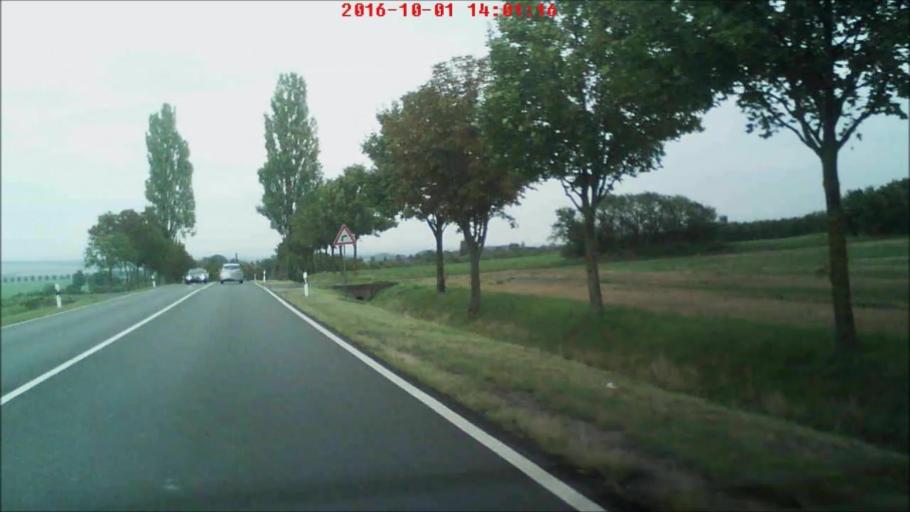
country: DE
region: Thuringia
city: Umpferstedt
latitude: 50.9829
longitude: 11.4217
